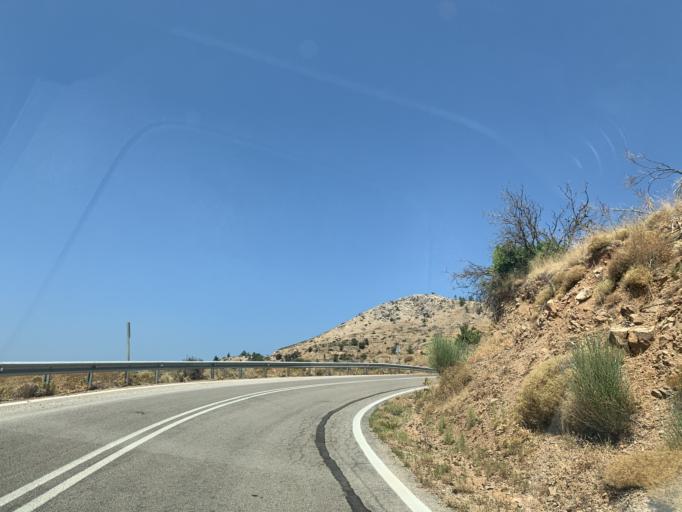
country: GR
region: North Aegean
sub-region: Chios
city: Vrontados
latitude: 38.4513
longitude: 25.9778
